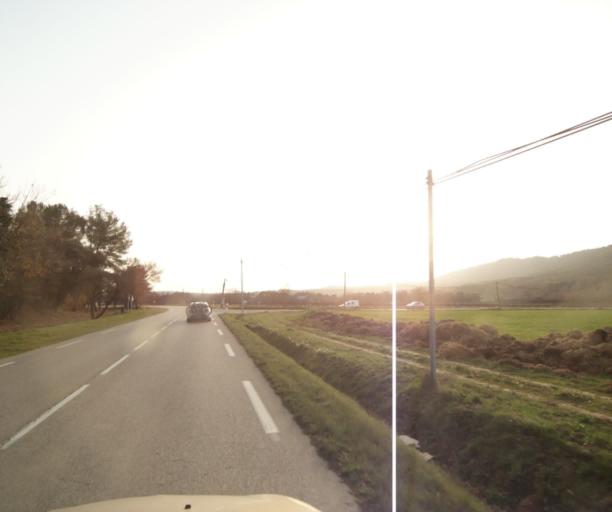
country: FR
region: Provence-Alpes-Cote d'Azur
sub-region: Departement des Bouches-du-Rhone
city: Rognes
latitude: 43.6959
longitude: 5.3449
